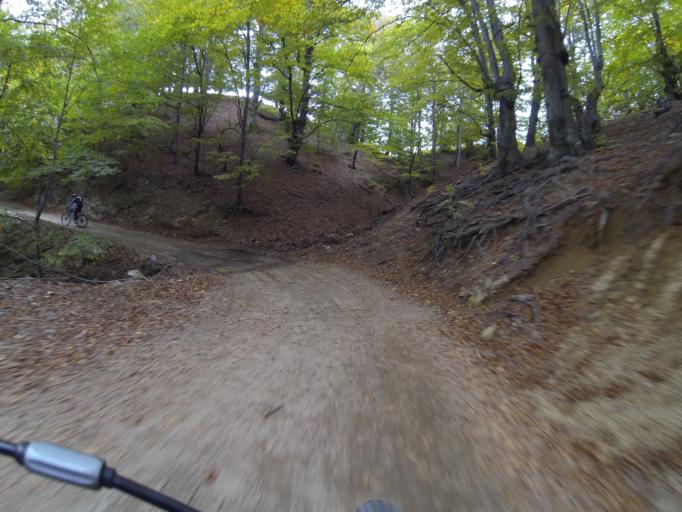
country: RO
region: Gorj
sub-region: Comuna Tismana
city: Sohodol
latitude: 45.0730
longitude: 22.8634
